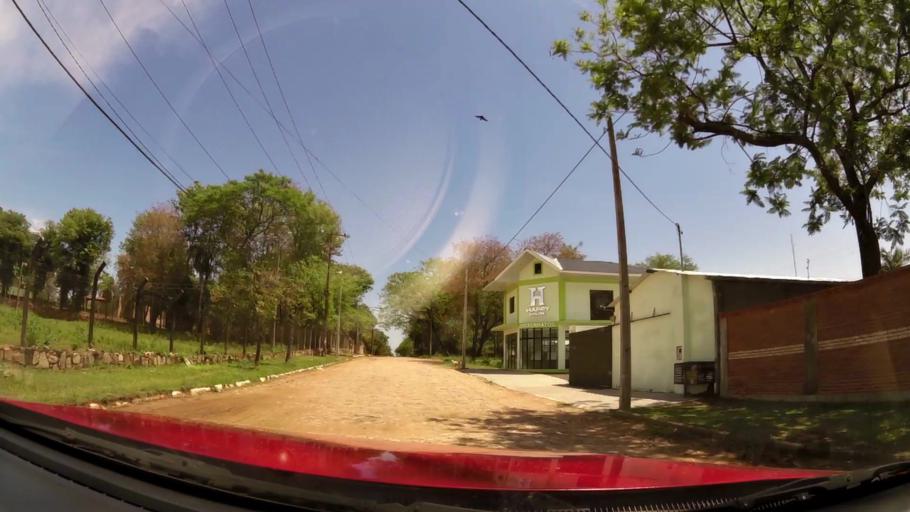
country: PY
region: Central
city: Colonia Mariano Roque Alonso
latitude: -25.2101
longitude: -57.5454
